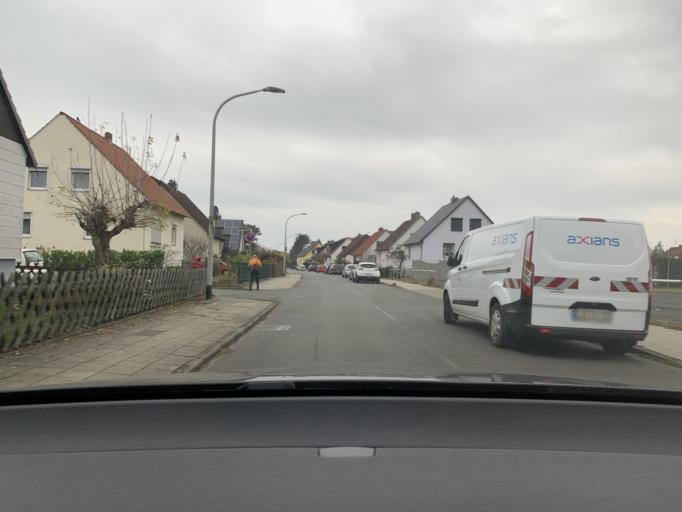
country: DE
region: Lower Saxony
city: Vordorf
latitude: 52.3214
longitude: 10.5120
